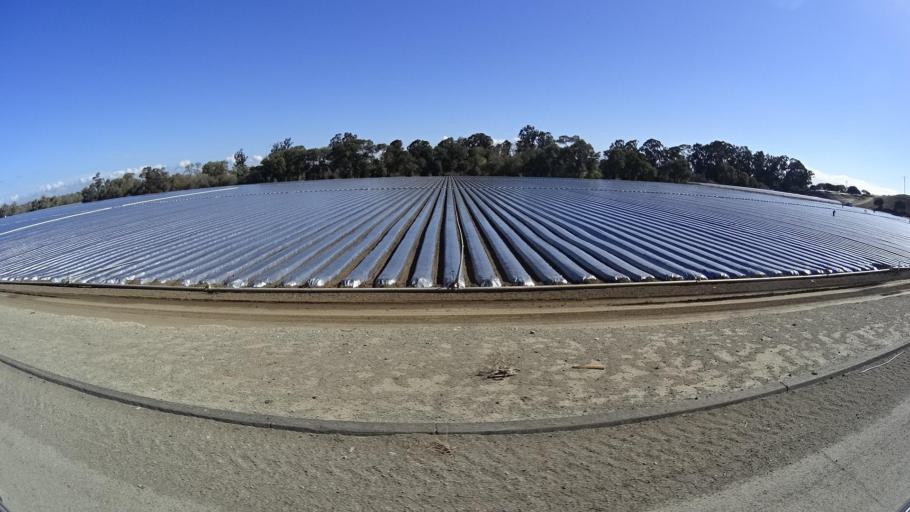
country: US
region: California
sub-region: Monterey County
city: Salinas
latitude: 36.6345
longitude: -121.6997
